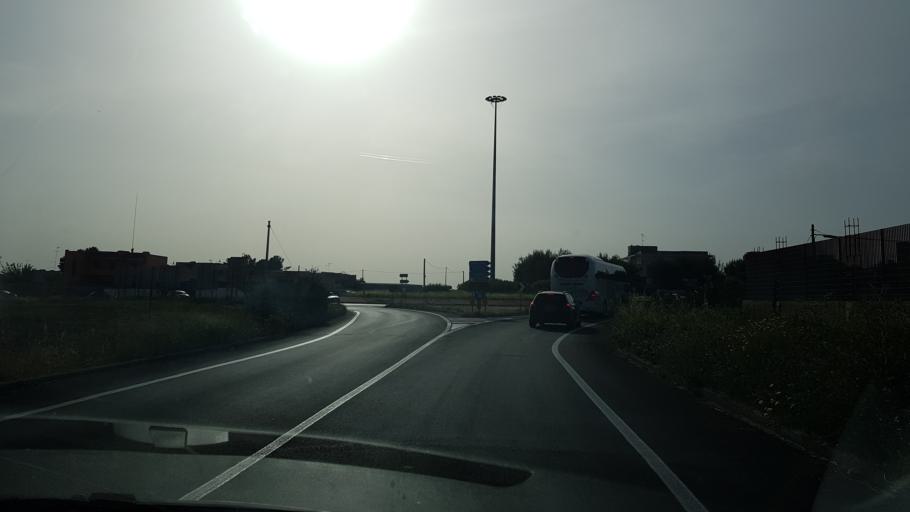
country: IT
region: Apulia
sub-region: Provincia di Lecce
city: Porto Cesareo
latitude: 40.2949
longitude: 17.8566
